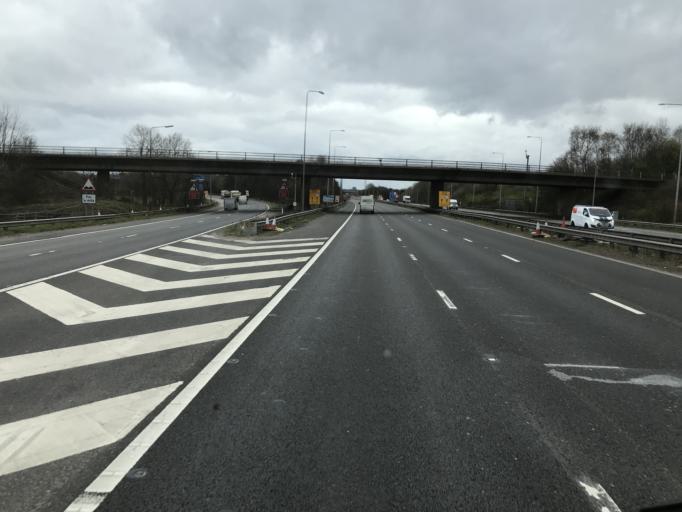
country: GB
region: England
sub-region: Warrington
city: Croft
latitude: 53.4240
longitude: -2.5702
